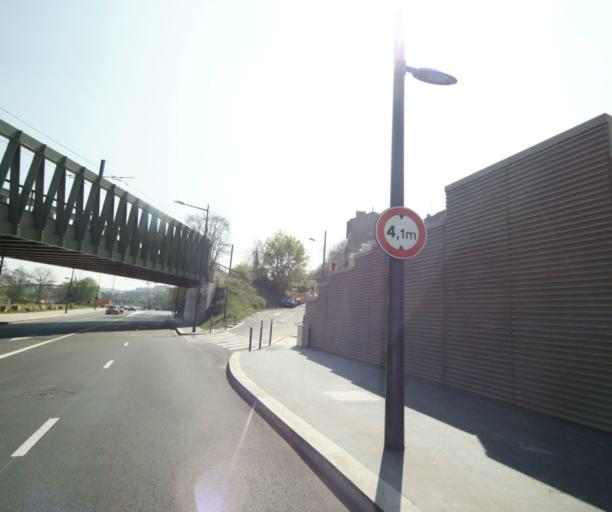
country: FR
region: Ile-de-France
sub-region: Departement des Hauts-de-Seine
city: Meudon
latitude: 48.8229
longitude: 2.2305
